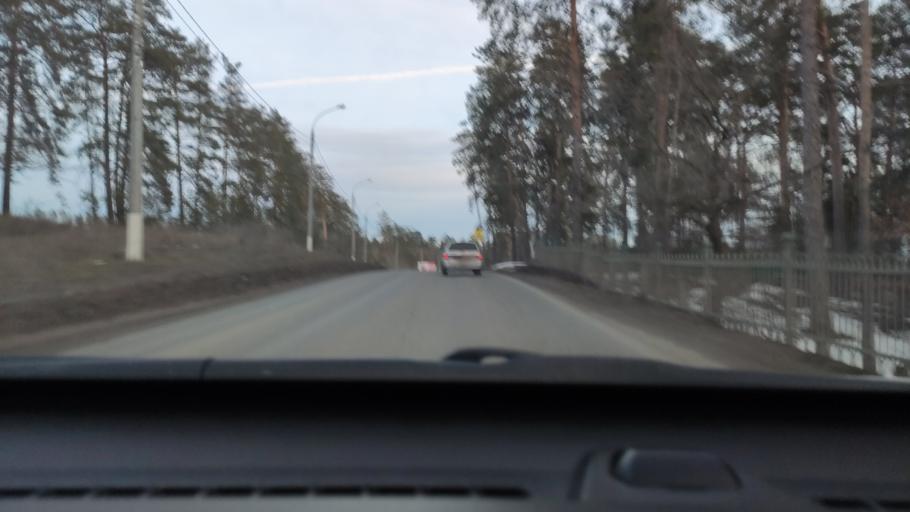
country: RU
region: Samara
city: Tol'yatti
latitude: 53.4840
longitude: 49.3127
